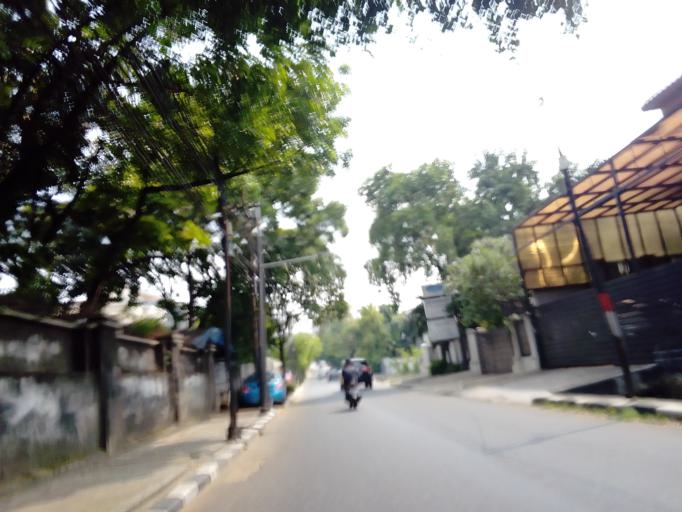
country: ID
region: Jakarta Raya
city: Jakarta
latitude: -6.2577
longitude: 106.7993
